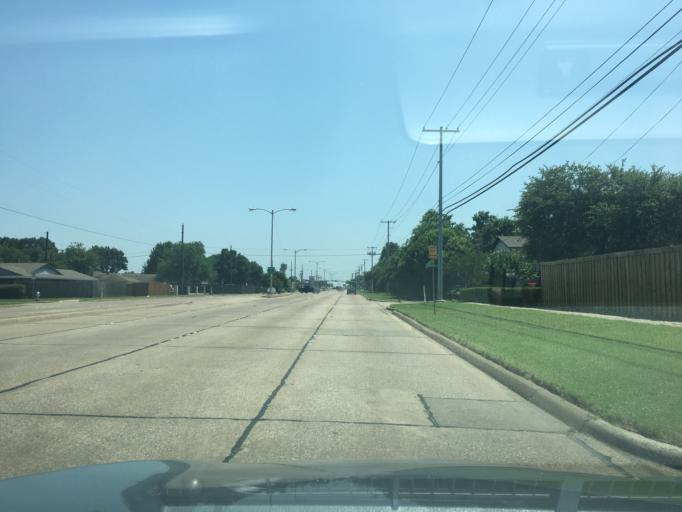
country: US
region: Texas
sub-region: Dallas County
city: Richardson
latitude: 32.9207
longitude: -96.7004
